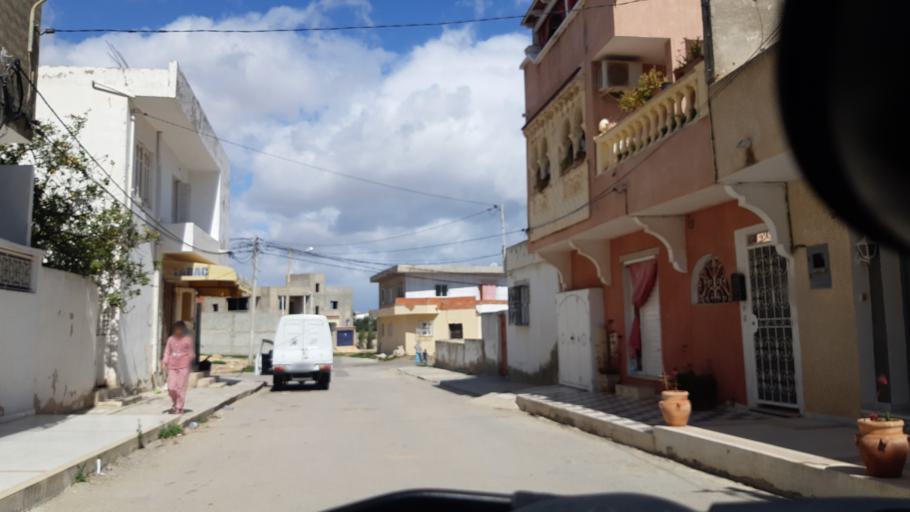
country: TN
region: Susah
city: Akouda
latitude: 35.8917
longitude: 10.5341
